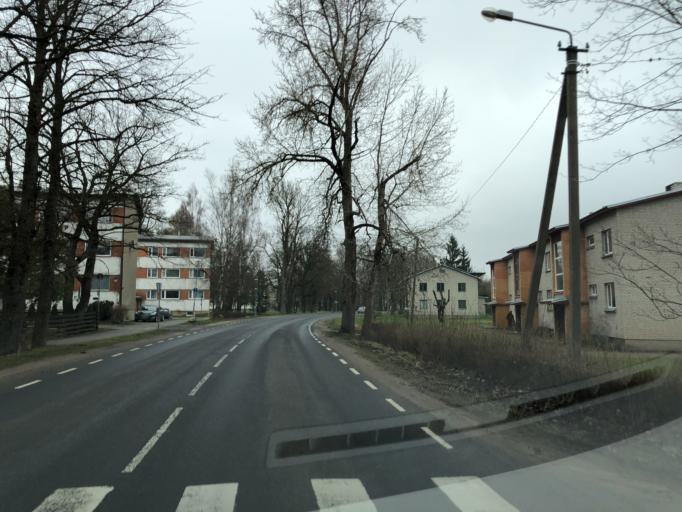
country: EE
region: Laeaene-Virumaa
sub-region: Vaeike-Maarja vald
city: Vaike-Maarja
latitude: 59.1248
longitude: 26.2487
